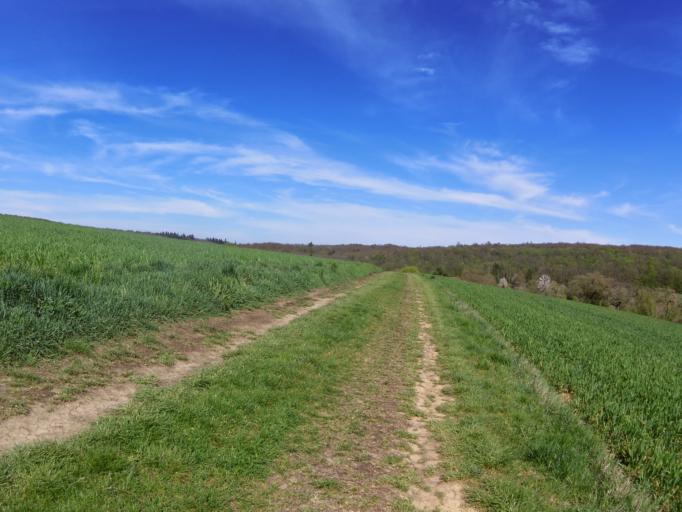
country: DE
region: Bavaria
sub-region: Regierungsbezirk Unterfranken
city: Rimpar
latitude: 49.8507
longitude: 9.9796
